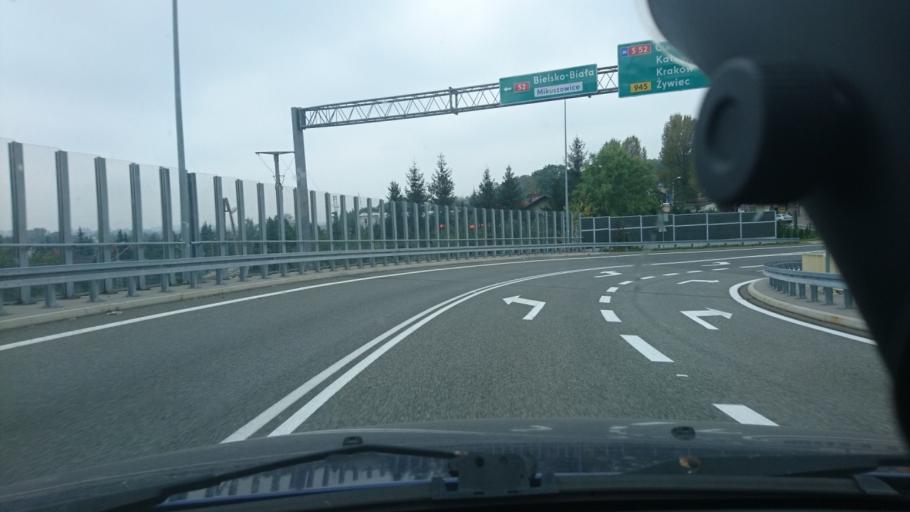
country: PL
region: Silesian Voivodeship
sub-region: Powiat bielski
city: Bystra
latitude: 49.7889
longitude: 19.0697
